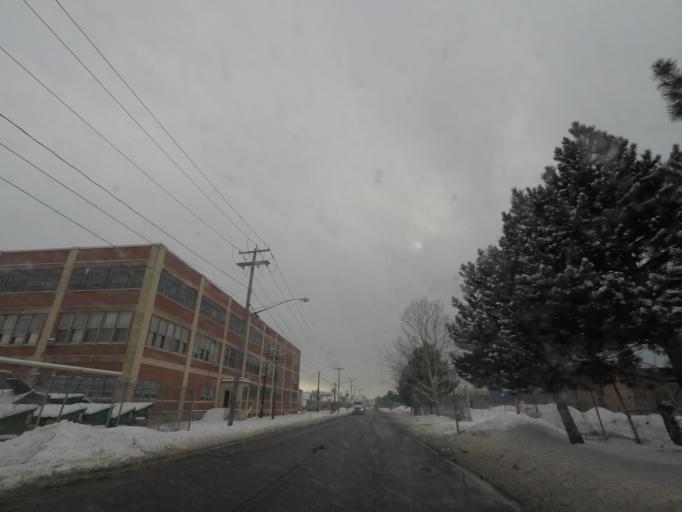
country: US
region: New York
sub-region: Rensselaer County
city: Rensselaer
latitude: 42.6340
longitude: -73.7561
